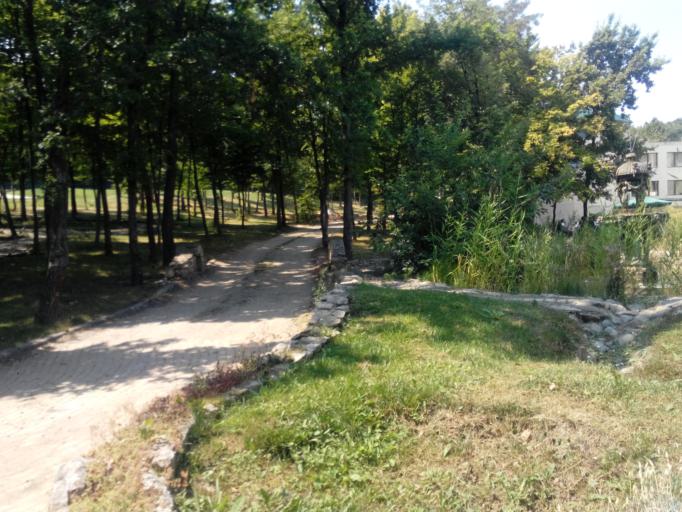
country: RO
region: Cluj
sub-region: Comuna Baciu
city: Baciu
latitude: 46.8107
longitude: 23.4863
